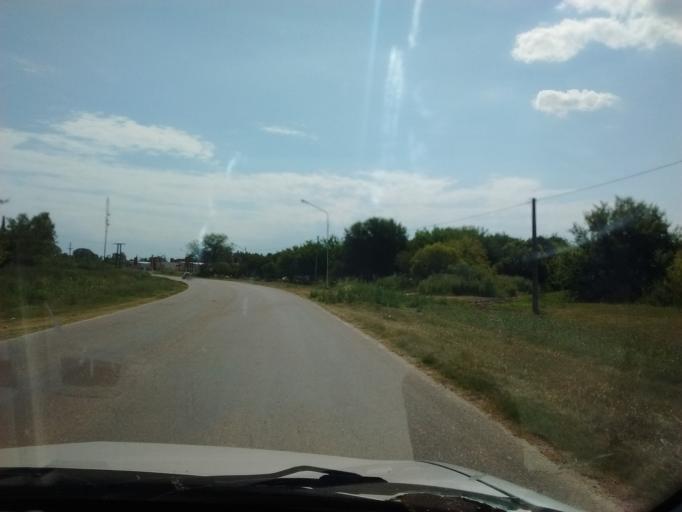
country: AR
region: Entre Rios
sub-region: Departamento de Victoria
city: Victoria
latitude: -32.6045
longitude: -60.1528
